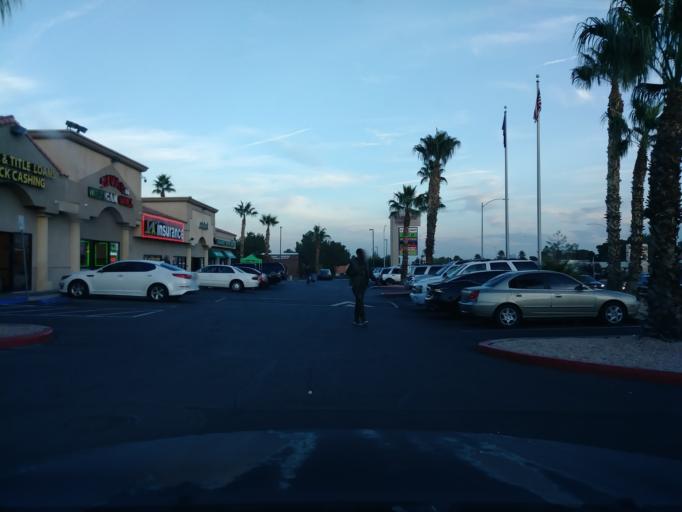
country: US
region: Nevada
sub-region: Clark County
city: Spring Valley
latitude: 36.1594
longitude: -115.2429
